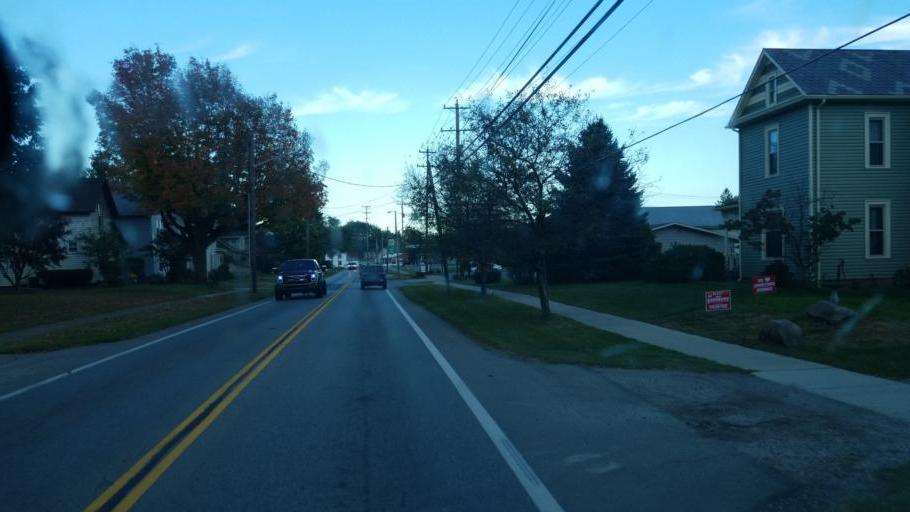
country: US
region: Ohio
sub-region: Licking County
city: Johnstown
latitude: 40.1507
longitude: -82.6920
